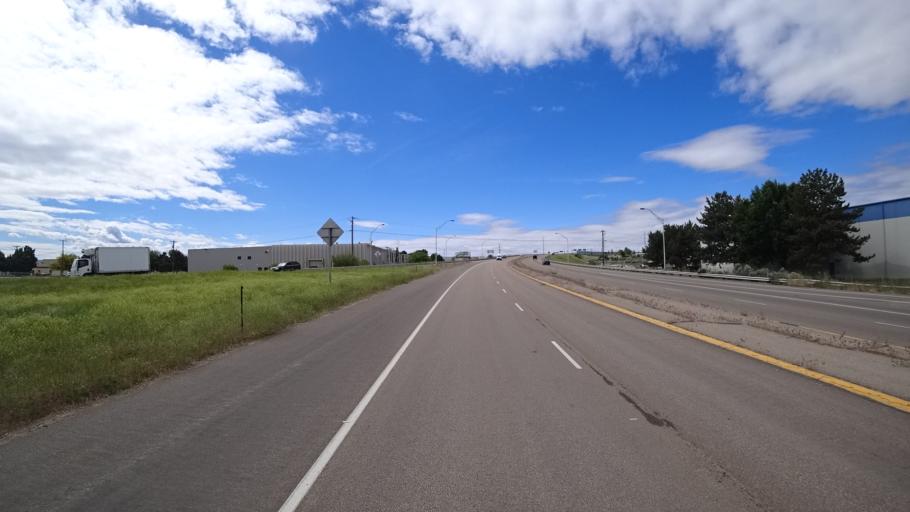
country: US
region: Idaho
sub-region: Ada County
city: Boise
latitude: 43.5723
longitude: -116.1936
